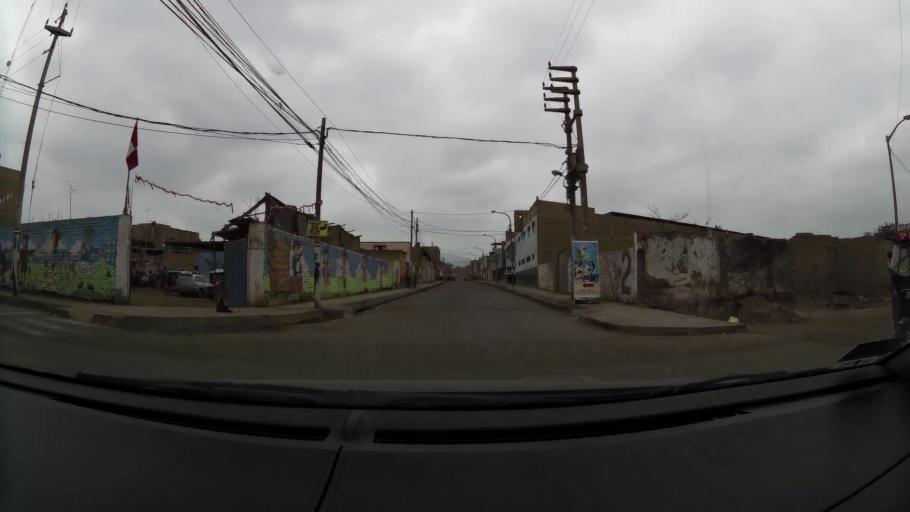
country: PE
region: Lima
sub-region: Provincia de Huaral
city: Huaral
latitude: -11.4979
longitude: -77.2028
